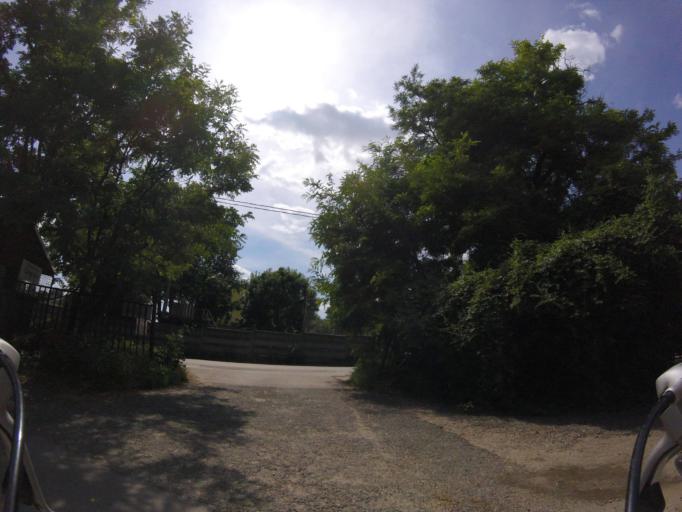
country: HU
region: Pest
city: Budaors
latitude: 47.4457
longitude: 18.9865
